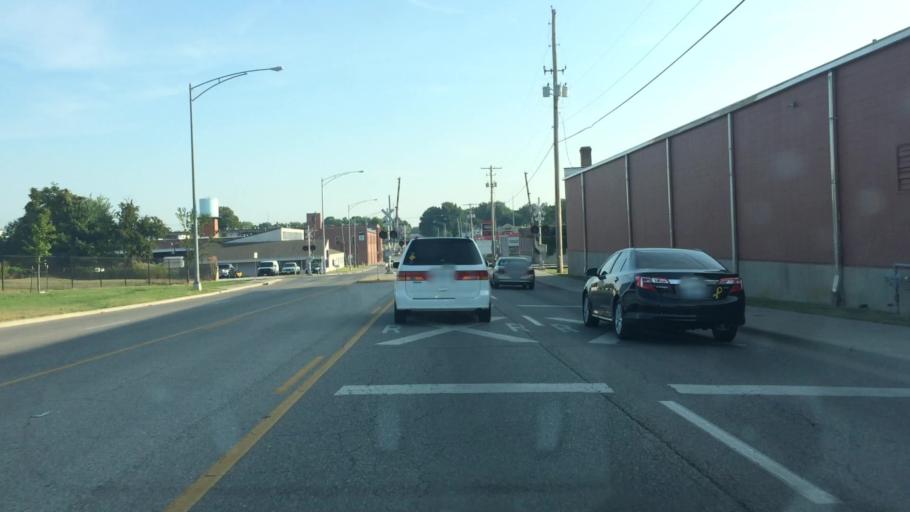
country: US
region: Missouri
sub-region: Greene County
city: Springfield
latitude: 37.2114
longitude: -93.2758
